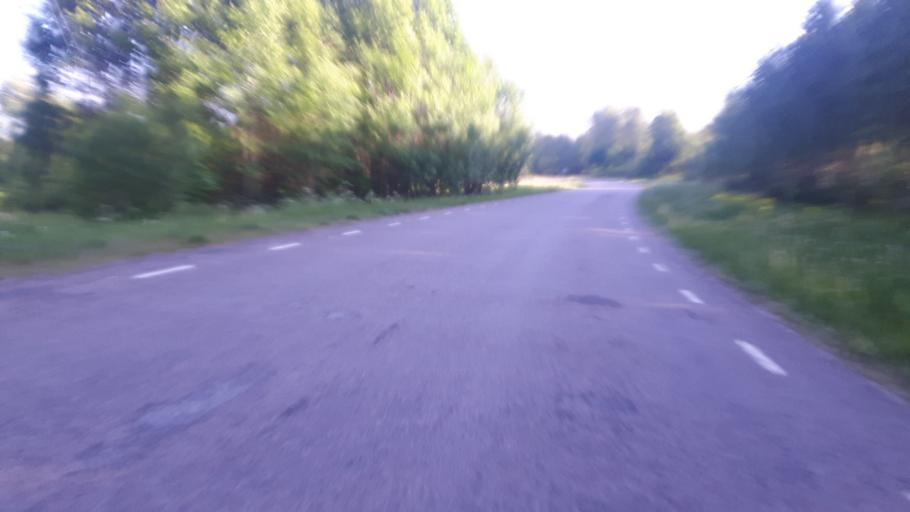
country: EE
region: Raplamaa
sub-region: Kehtna vald
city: Kehtna
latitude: 58.8911
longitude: 24.8783
